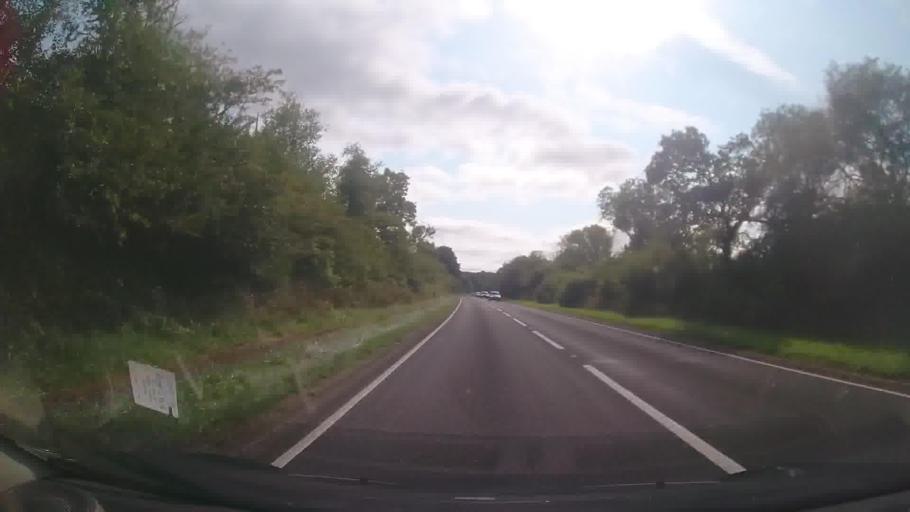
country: GB
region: Wales
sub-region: Pembrokeshire
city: Jeffreyston
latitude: 51.7122
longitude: -4.7627
